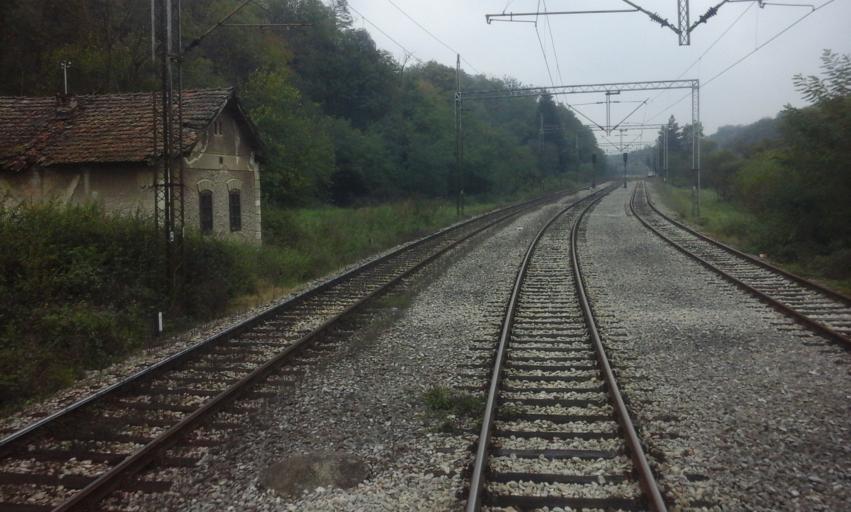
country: RS
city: Rusanj
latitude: 44.6443
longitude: 20.5334
